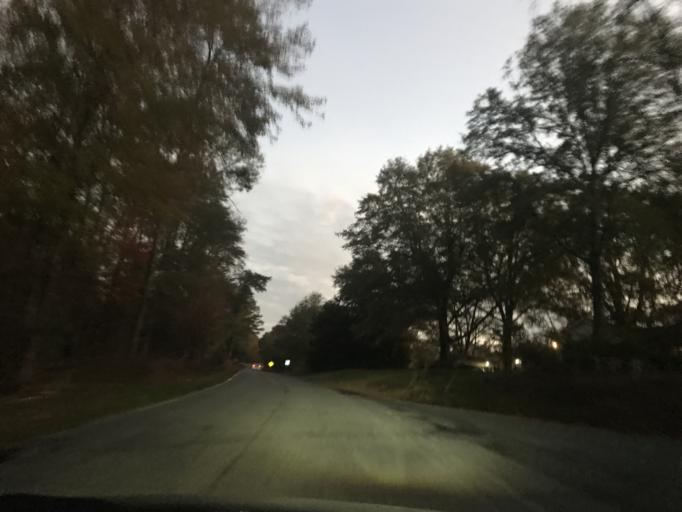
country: US
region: South Carolina
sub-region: Spartanburg County
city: Mayo
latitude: 35.0734
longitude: -81.9017
